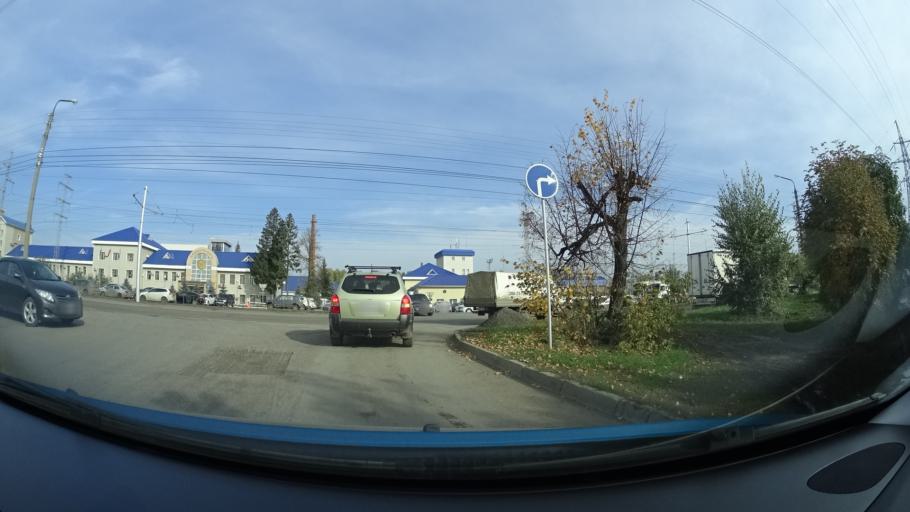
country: RU
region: Bashkortostan
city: Ufa
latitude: 54.7968
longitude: 56.0602
